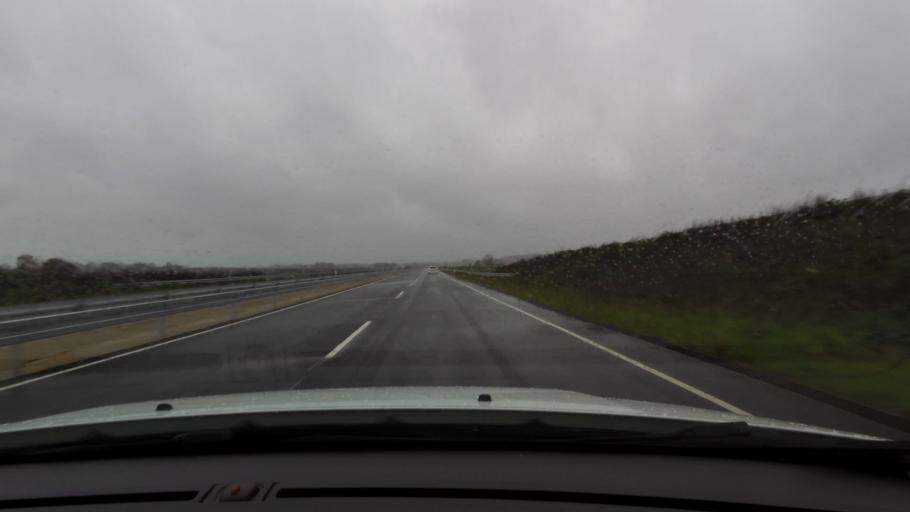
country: DK
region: Capital Region
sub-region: Frederikssund Kommune
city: Skibby
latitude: 55.7982
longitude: 11.9887
